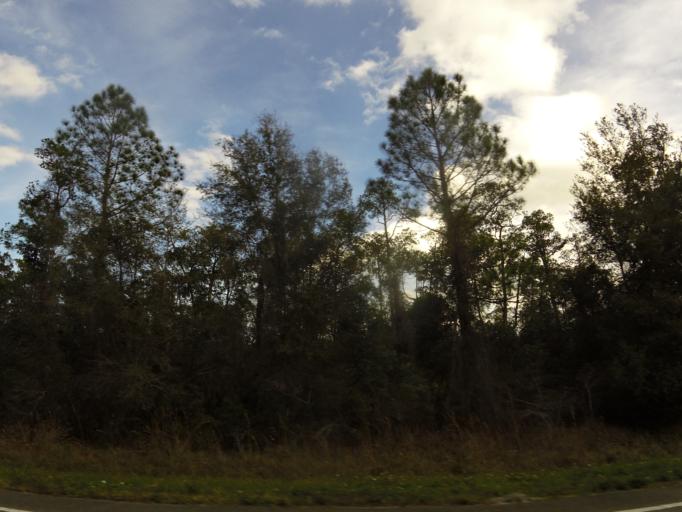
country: US
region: Florida
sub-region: Volusia County
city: De Leon Springs
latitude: 29.2441
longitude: -81.3255
